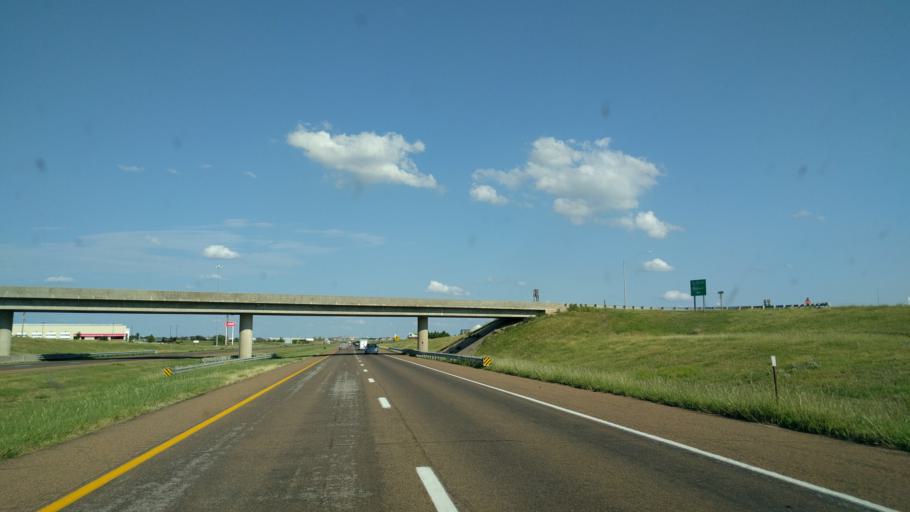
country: US
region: Kansas
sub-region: Ellis County
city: Hays
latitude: 38.9126
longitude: -99.3555
